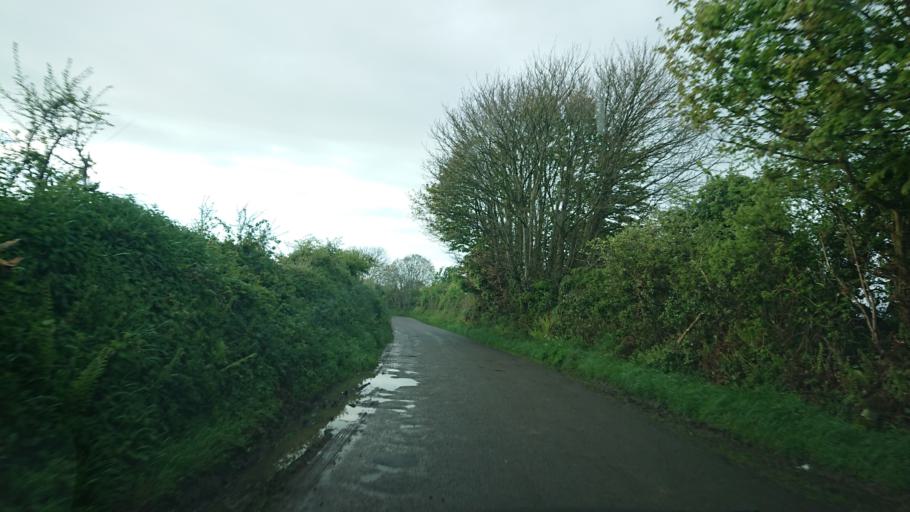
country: IE
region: Munster
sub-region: Waterford
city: Waterford
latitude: 52.2343
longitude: -7.1309
